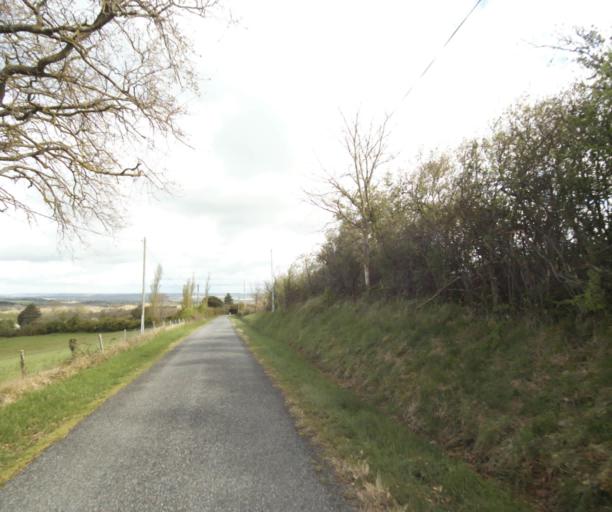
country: FR
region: Midi-Pyrenees
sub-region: Departement de l'Ariege
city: Saverdun
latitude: 43.2281
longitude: 1.5247
